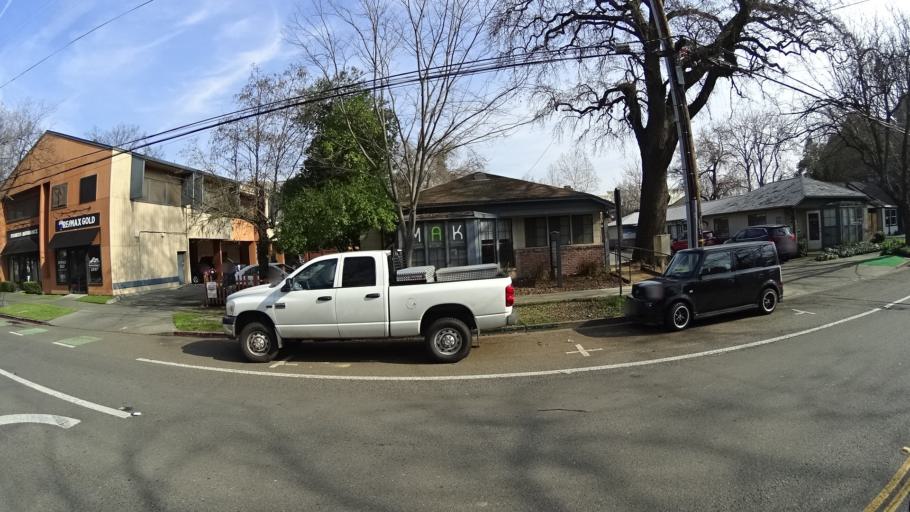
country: US
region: California
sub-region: Yolo County
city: Davis
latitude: 38.5470
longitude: -121.7410
